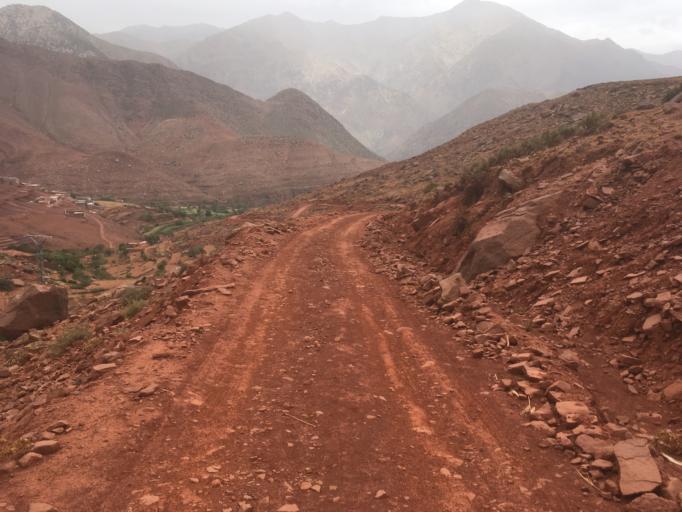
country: MA
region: Marrakech-Tensift-Al Haouz
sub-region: Al-Haouz
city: Tidili Mesfioua
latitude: 31.2797
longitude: -7.6750
